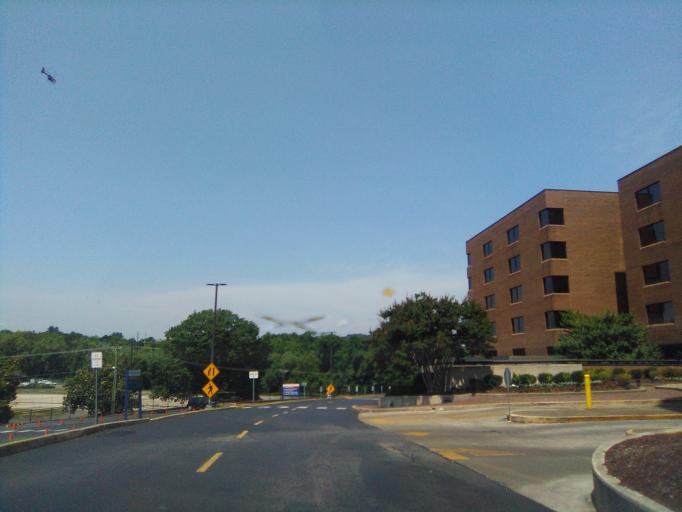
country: US
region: Tennessee
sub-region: Davidson County
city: Belle Meade
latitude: 36.1283
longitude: -86.8448
